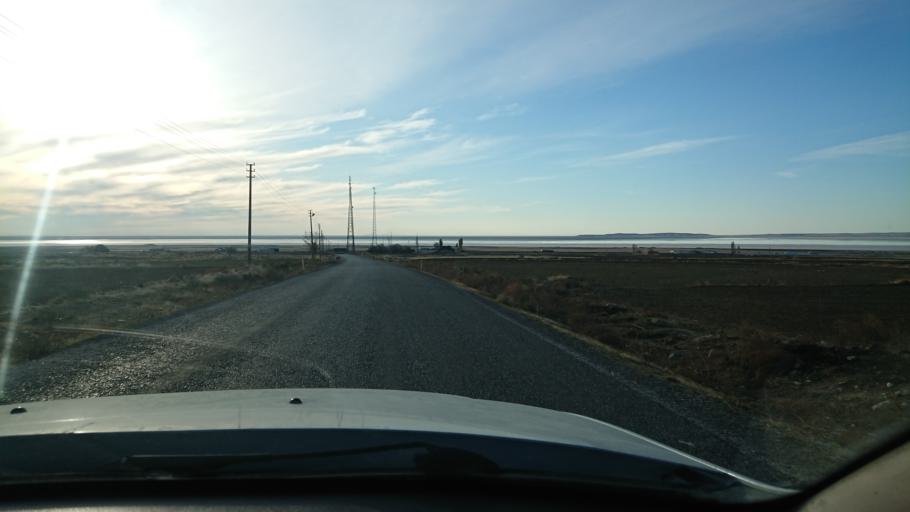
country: TR
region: Ankara
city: Sereflikochisar
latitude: 38.7432
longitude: 33.6729
